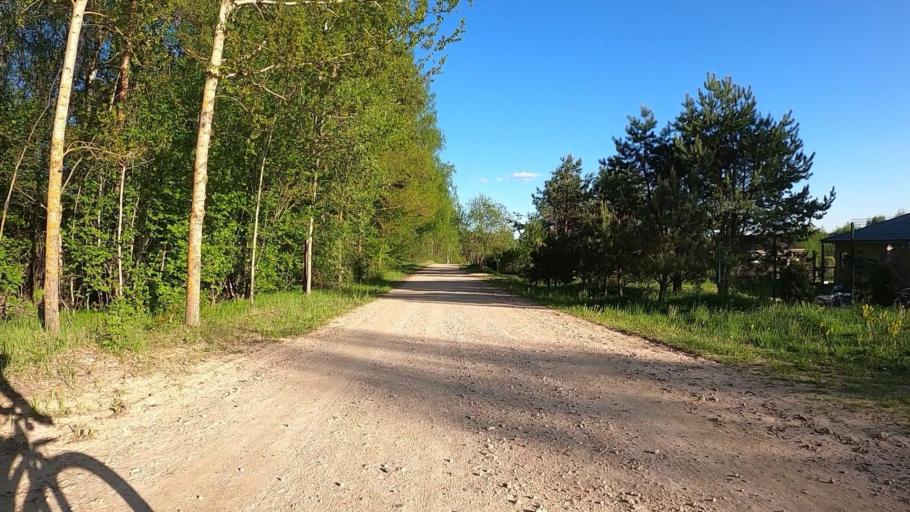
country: LV
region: Kekava
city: Kekava
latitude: 56.7751
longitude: 24.2855
